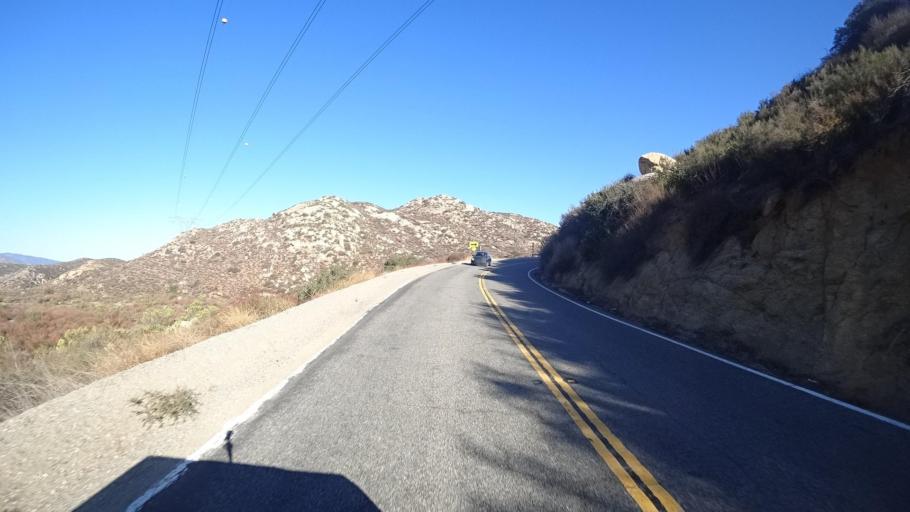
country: MX
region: Baja California
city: Tecate
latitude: 32.5990
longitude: -116.6433
